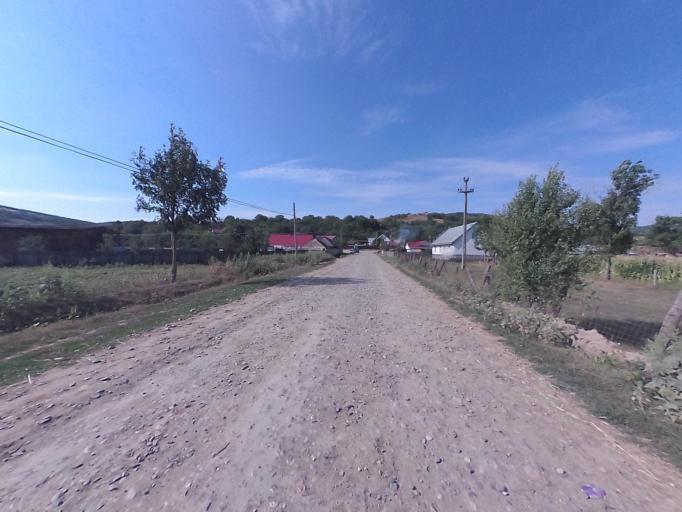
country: RO
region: Vaslui
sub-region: Comuna Osesti
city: Buda
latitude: 46.7605
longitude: 27.4264
